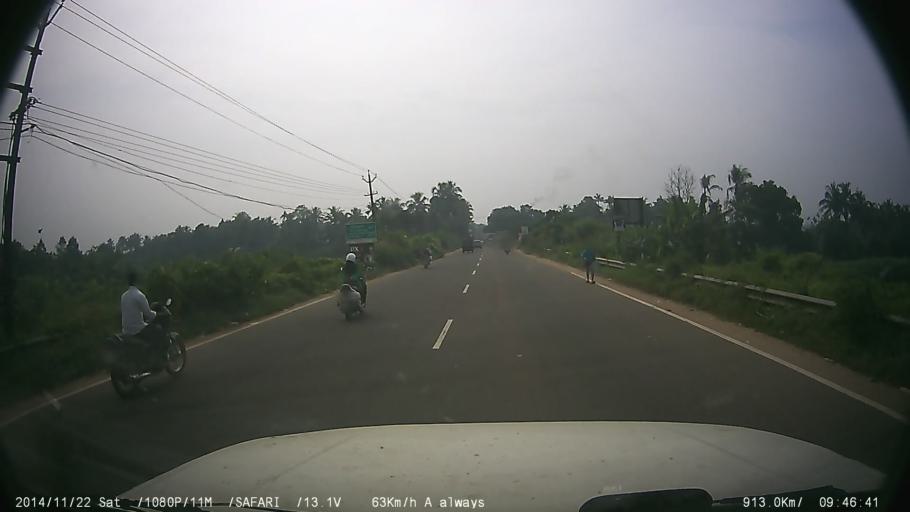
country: IN
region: Kerala
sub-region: Ernakulam
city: Perumpavur
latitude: 10.1346
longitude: 76.4684
